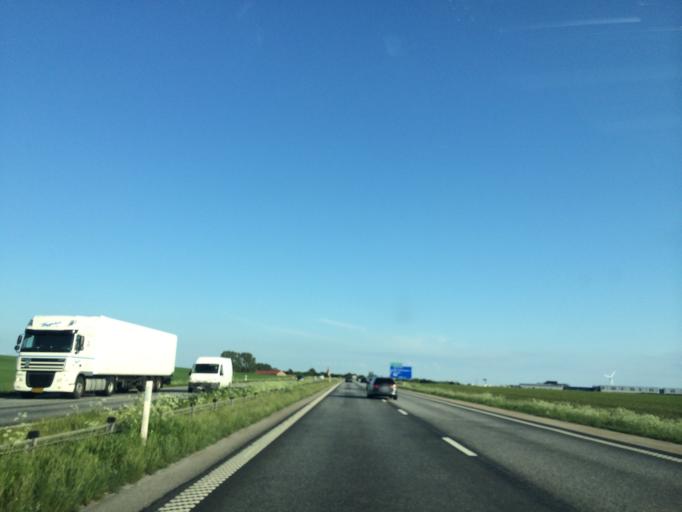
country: SE
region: Skane
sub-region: Landskrona
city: Landskrona
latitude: 55.8898
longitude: 12.8719
